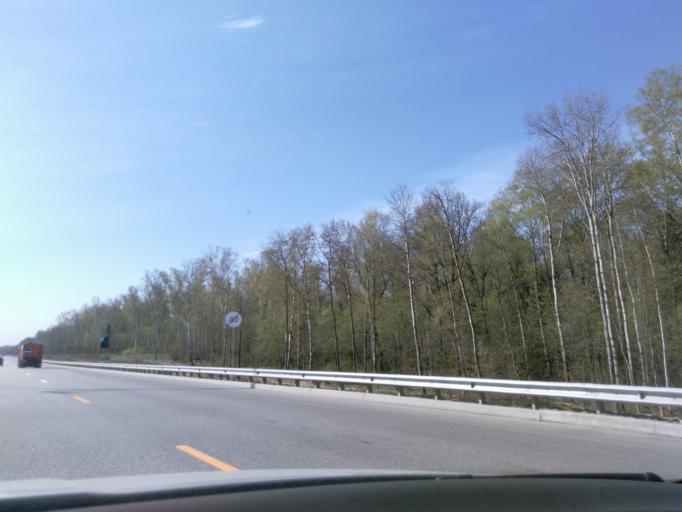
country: RU
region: Moscow
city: Khimki
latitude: 55.9319
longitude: 37.4518
